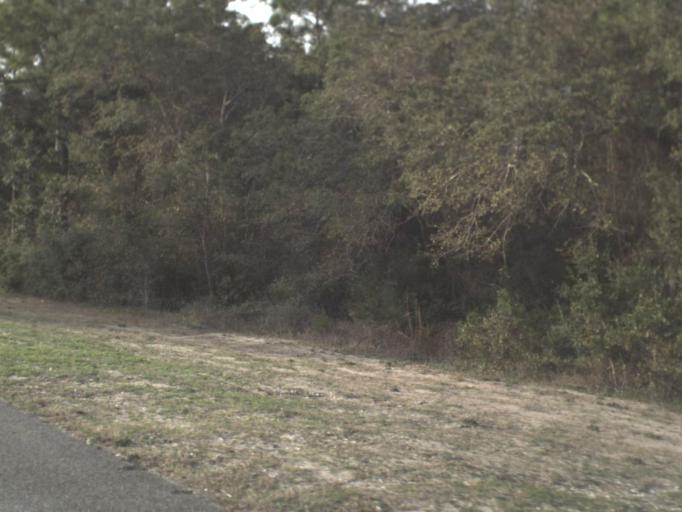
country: US
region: Florida
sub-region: Bay County
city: Mexico Beach
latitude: 29.9564
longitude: -85.4321
